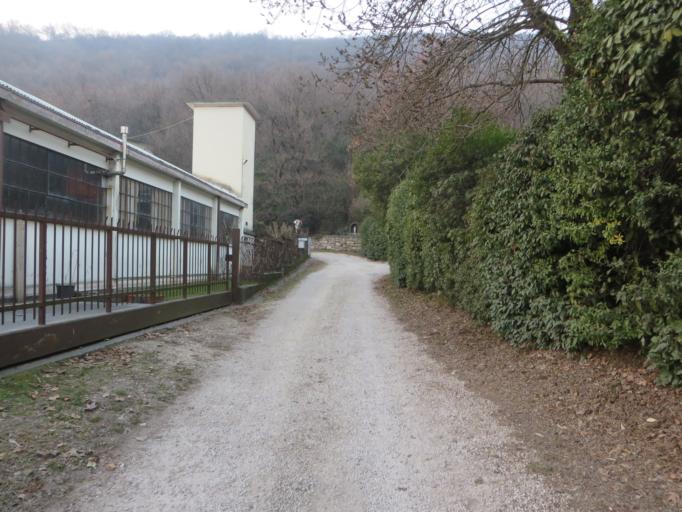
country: IT
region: Lombardy
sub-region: Provincia di Brescia
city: Prevalle
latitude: 45.5643
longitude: 10.4306
